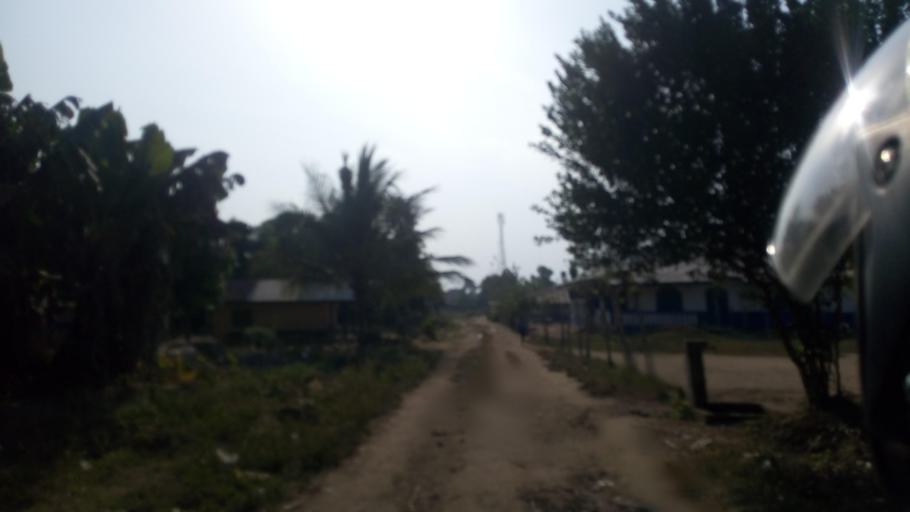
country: SL
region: Southern Province
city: Mogbwemo
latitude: 7.6118
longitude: -12.1775
